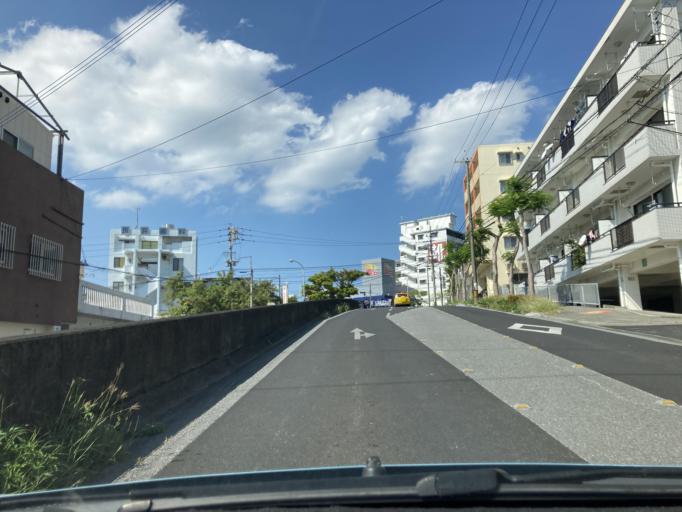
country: JP
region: Okinawa
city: Tomigusuku
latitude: 26.1993
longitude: 127.6983
